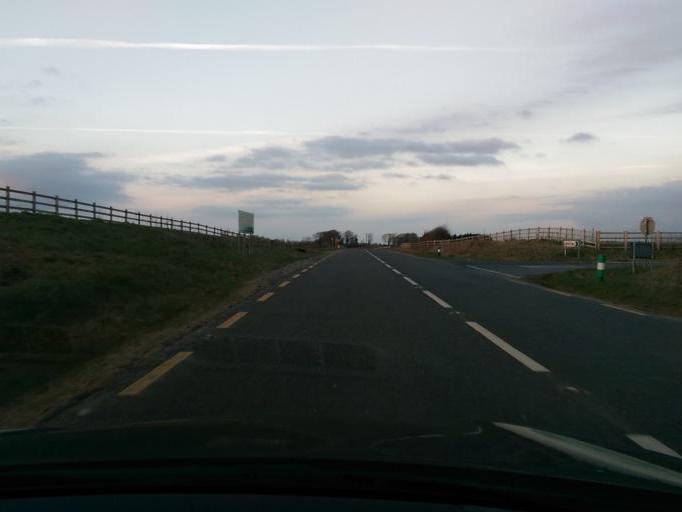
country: IE
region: Munster
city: Nenagh Bridge
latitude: 52.9512
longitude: -8.1421
